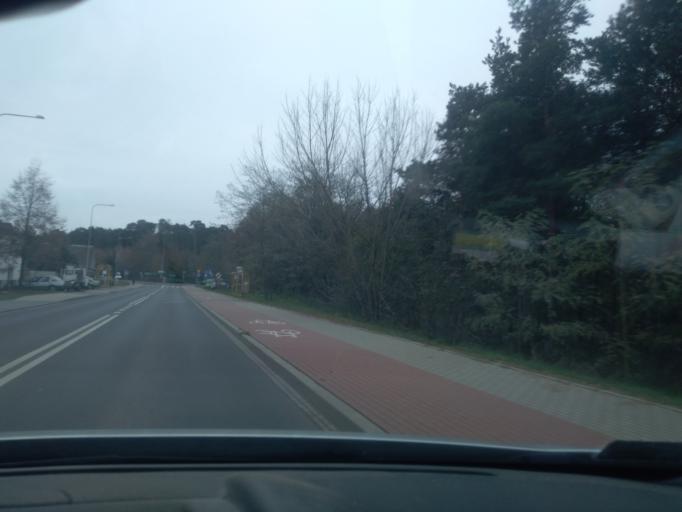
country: PL
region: Greater Poland Voivodeship
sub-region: Powiat poznanski
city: Murowana Goslina
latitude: 52.5421
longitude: 16.9725
